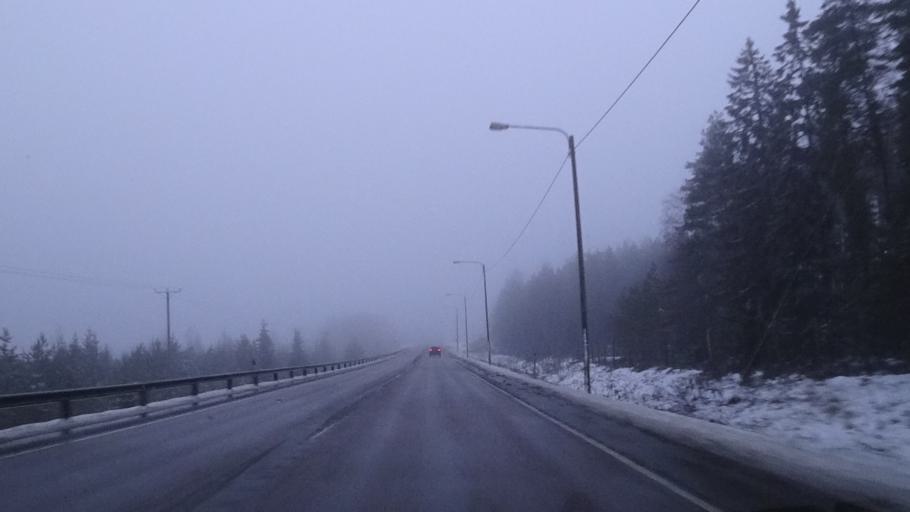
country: FI
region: Paijanne Tavastia
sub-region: Lahti
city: Hollola
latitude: 60.9872
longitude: 25.3989
